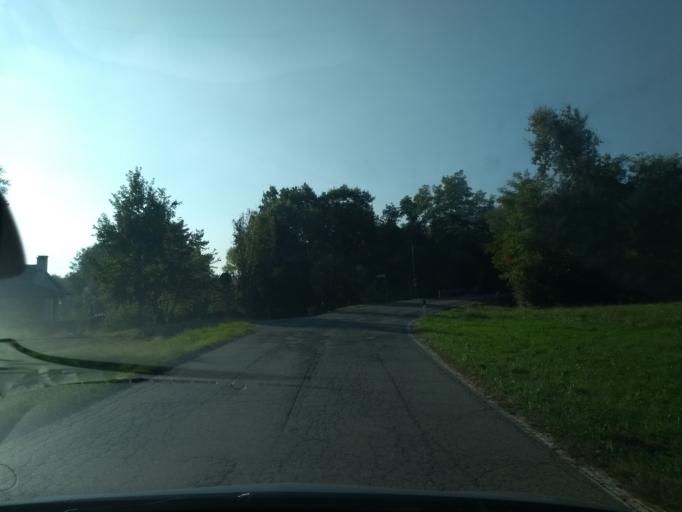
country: IT
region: Piedmont
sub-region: Provincia di Torino
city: Monasterolo
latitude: 45.2388
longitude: 7.5122
